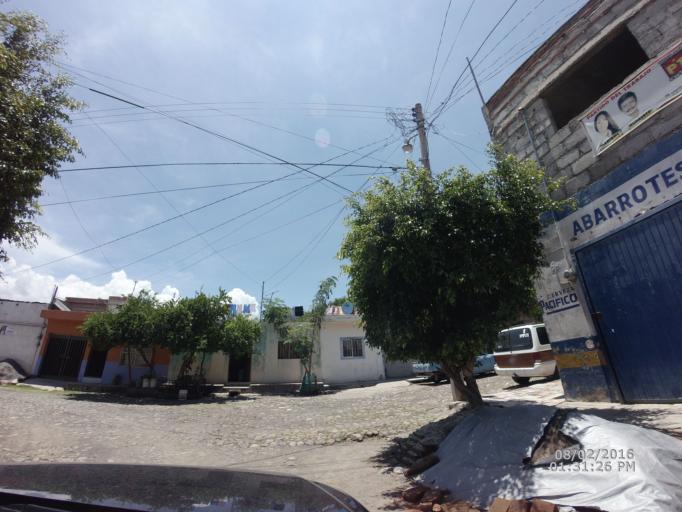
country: MX
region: Nayarit
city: Ixtlan del Rio
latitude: 21.0424
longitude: -104.3747
